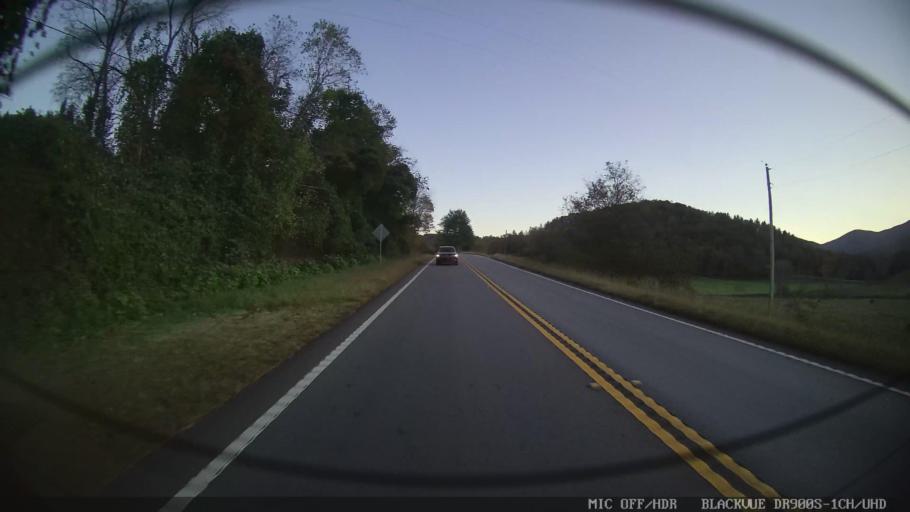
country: US
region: Georgia
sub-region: Union County
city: Blairsville
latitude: 34.8066
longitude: -83.9004
